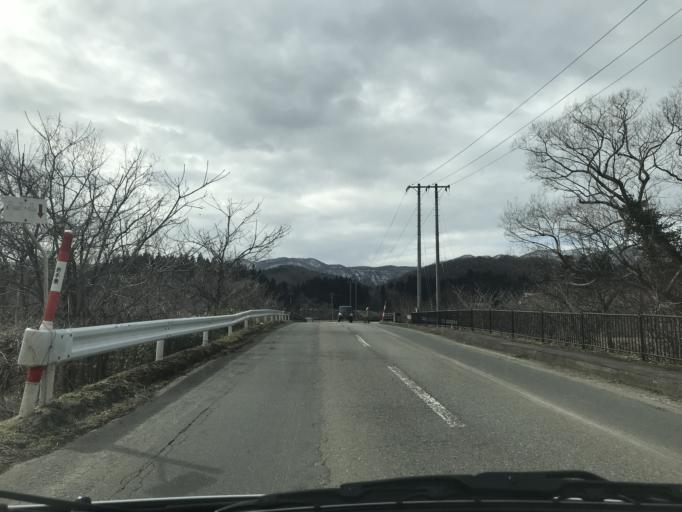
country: JP
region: Iwate
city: Hanamaki
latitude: 39.3405
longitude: 140.9804
